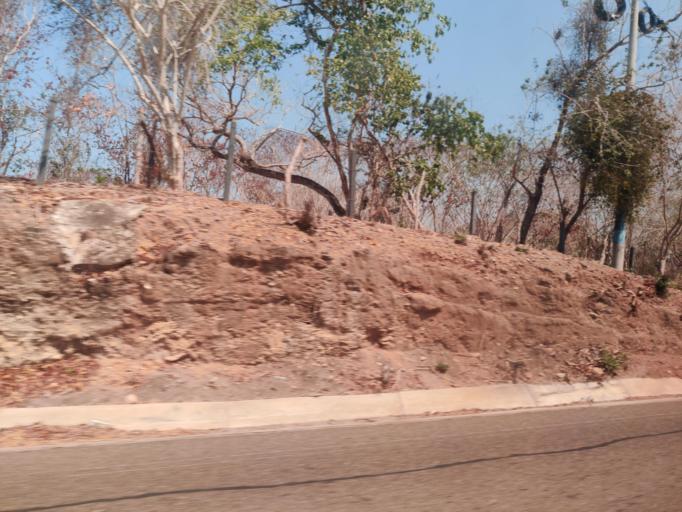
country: CO
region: Bolivar
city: Turbana
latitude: 10.2174
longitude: -75.5883
